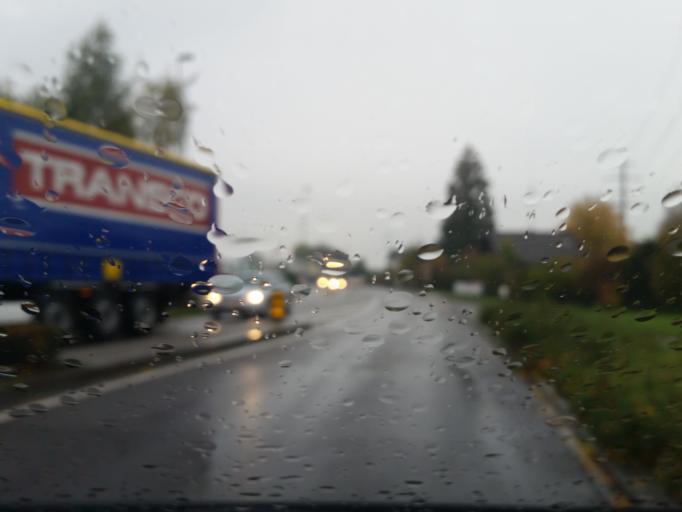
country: CH
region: Thurgau
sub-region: Weinfelden District
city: Maerstetten-Dorf
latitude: 47.5831
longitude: 9.0602
